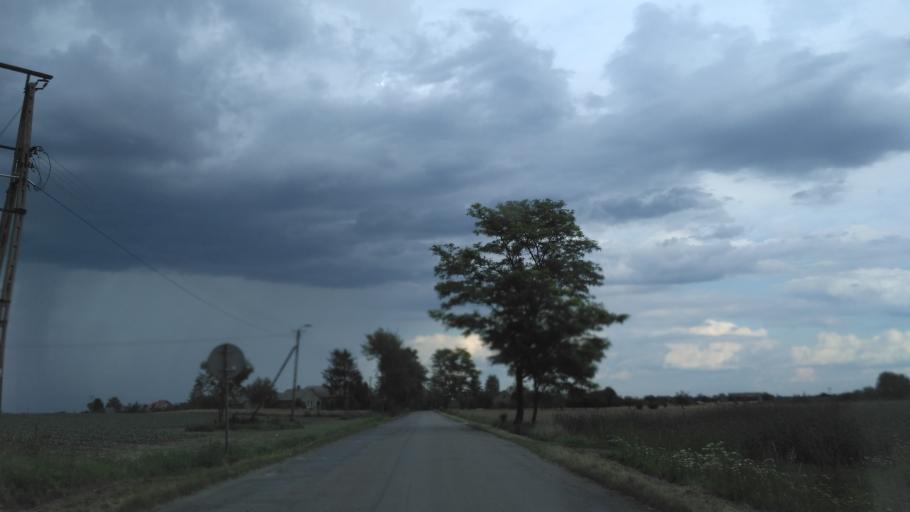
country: PL
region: Lublin Voivodeship
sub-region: Powiat leczynski
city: Milejow
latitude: 51.2167
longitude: 22.8924
